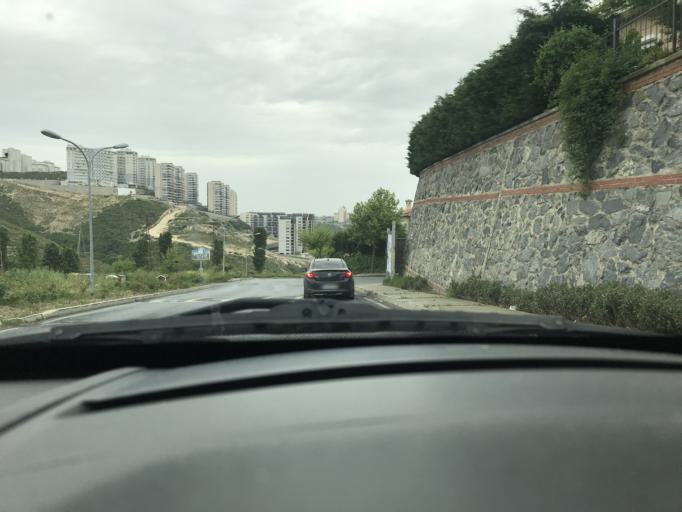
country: TR
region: Istanbul
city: Esenyurt
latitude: 41.0893
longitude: 28.6823
